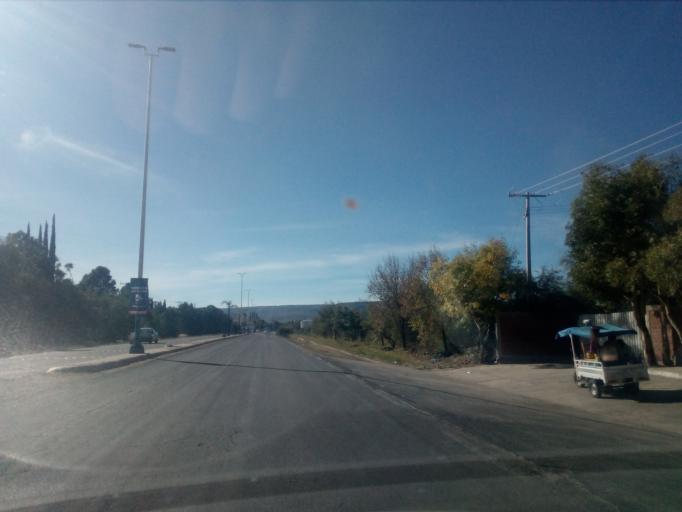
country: MX
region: Durango
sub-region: Durango
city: Sebastian Lerdo de Tejada
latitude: 23.9803
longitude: -104.6643
